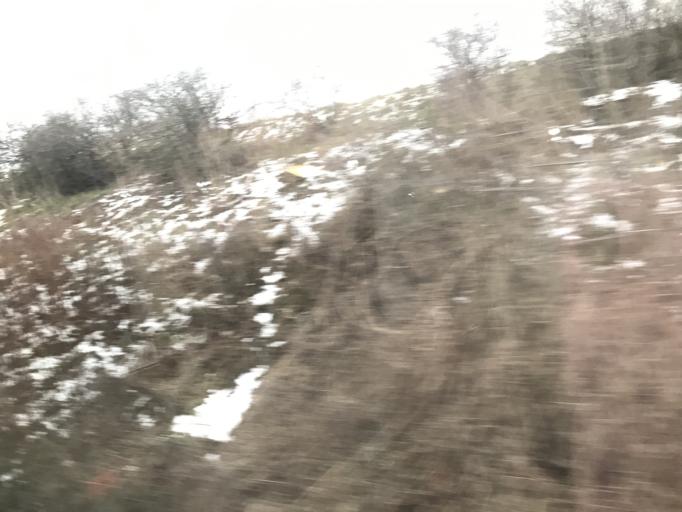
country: AT
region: Burgenland
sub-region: Politischer Bezirk Neusiedl am See
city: Parndorf
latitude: 48.0019
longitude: 16.8288
